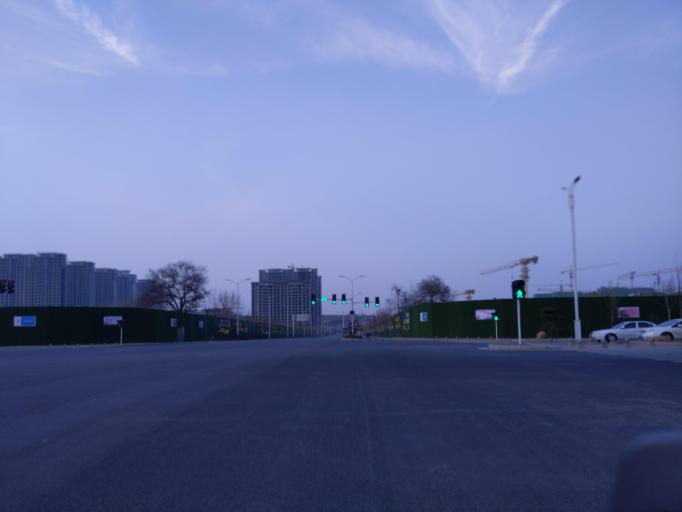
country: CN
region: Henan Sheng
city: Puyang
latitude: 35.8105
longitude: 115.0116
